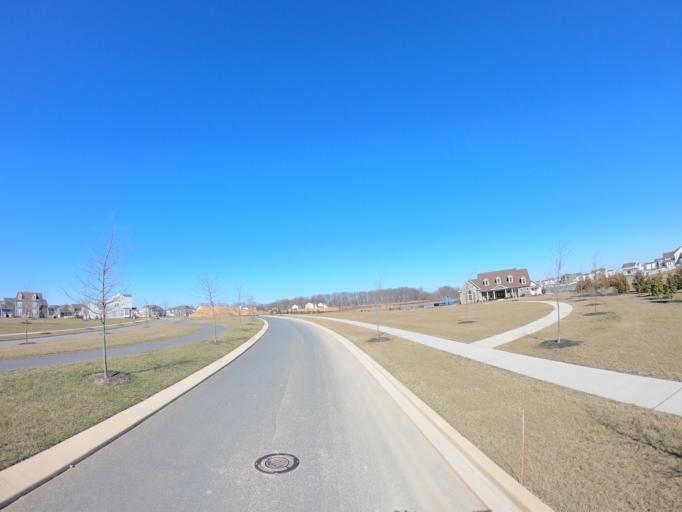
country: US
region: Delaware
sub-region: New Castle County
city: Middletown
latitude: 39.5144
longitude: -75.6664
